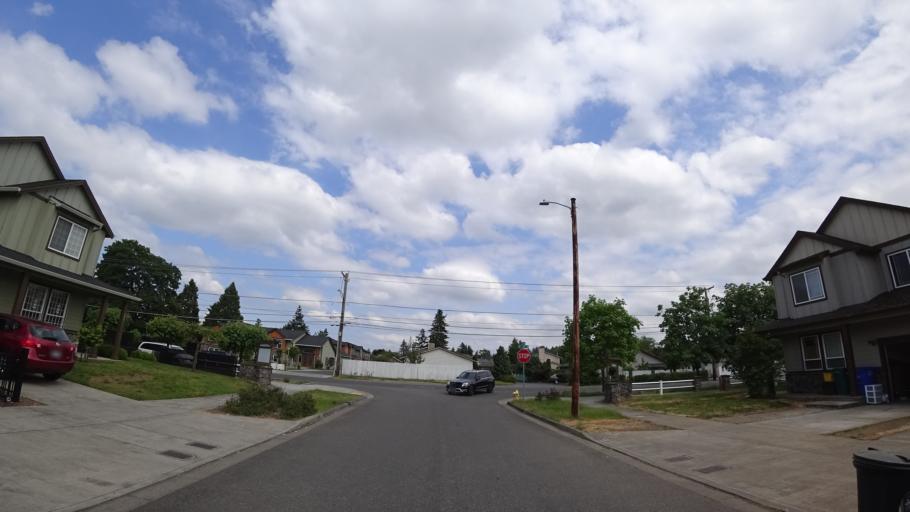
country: US
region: Oregon
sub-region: Multnomah County
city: Gresham
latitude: 45.5063
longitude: -122.4851
